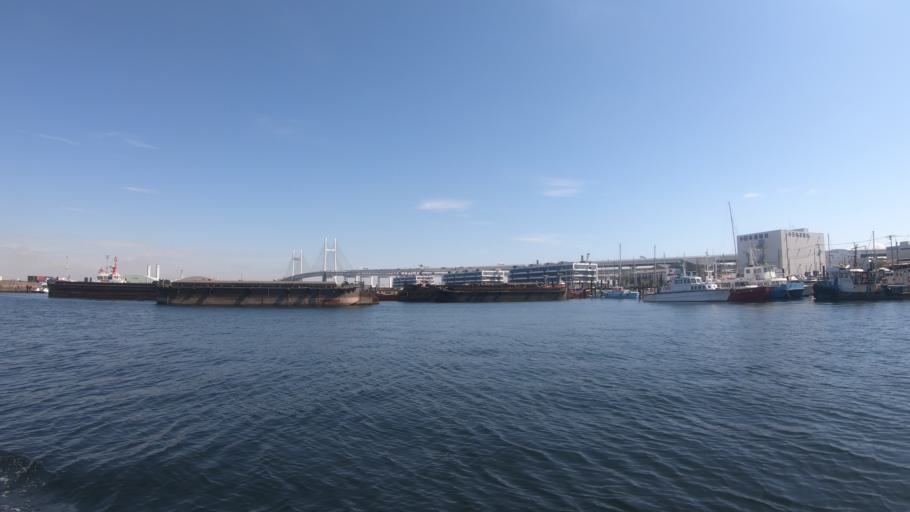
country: JP
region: Kanagawa
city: Yokohama
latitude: 35.4433
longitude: 139.6604
